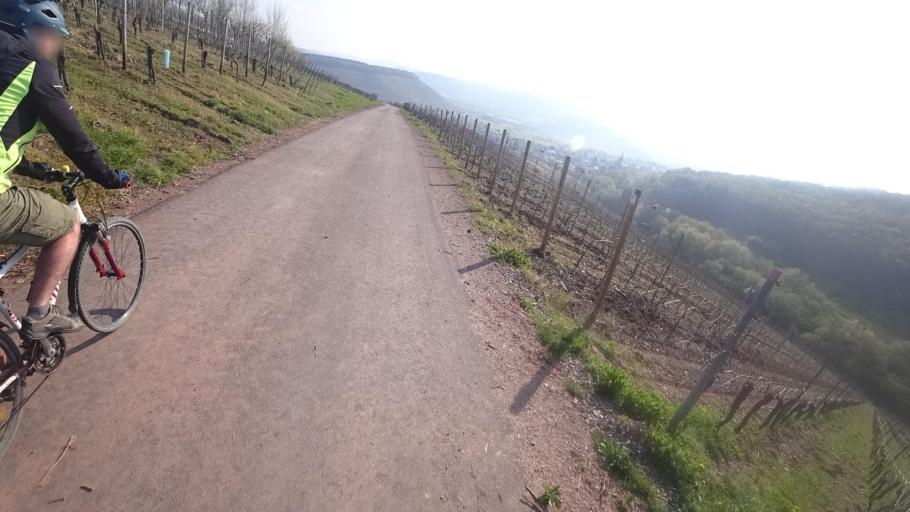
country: DE
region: Rheinland-Pfalz
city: Ayl
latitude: 49.6274
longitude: 6.5449
